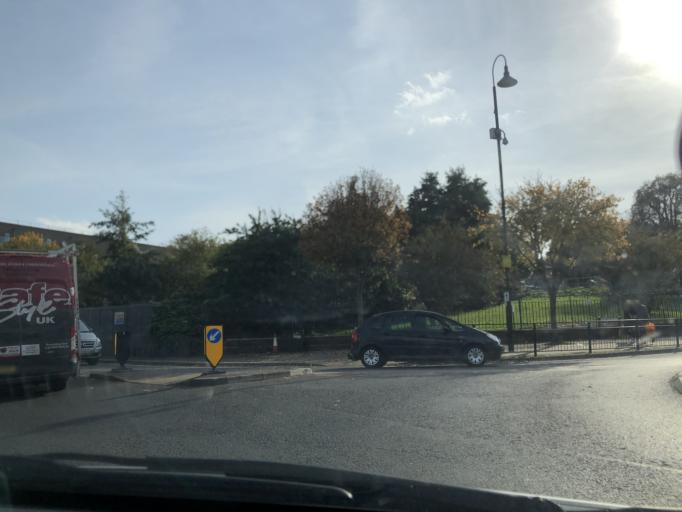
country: GB
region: England
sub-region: Greater London
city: Erith
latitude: 51.4503
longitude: 0.1821
